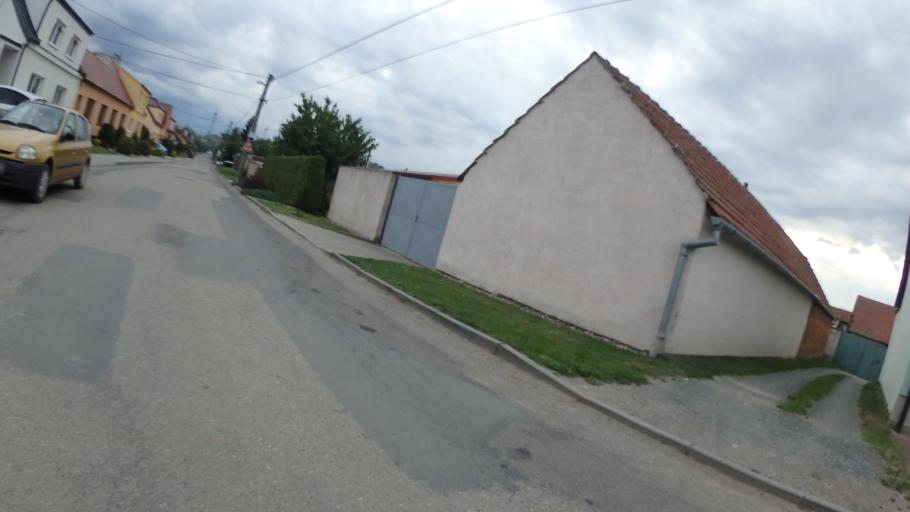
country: CZ
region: South Moravian
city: Ostopovice
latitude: 49.1400
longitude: 16.5551
